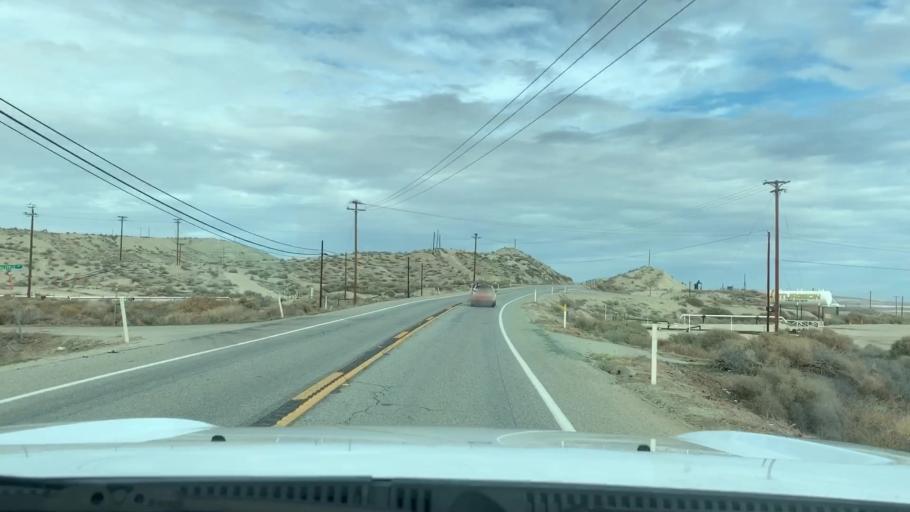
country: US
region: California
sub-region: Kern County
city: Maricopa
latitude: 35.0758
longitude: -119.4019
